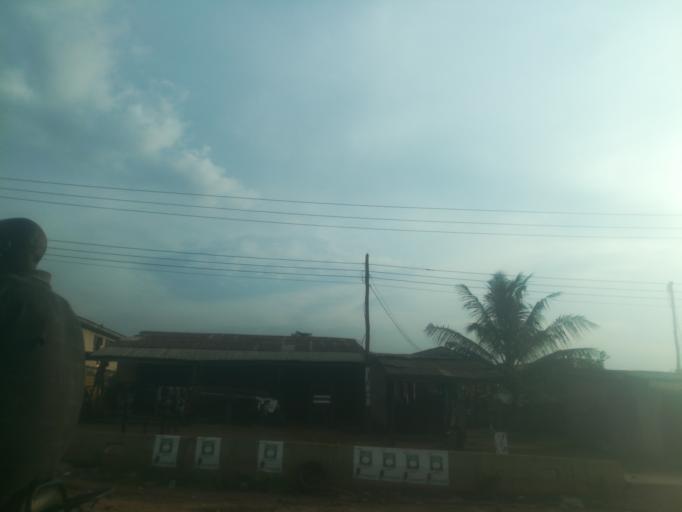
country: NG
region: Ogun
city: Abeokuta
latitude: 7.1671
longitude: 3.3022
